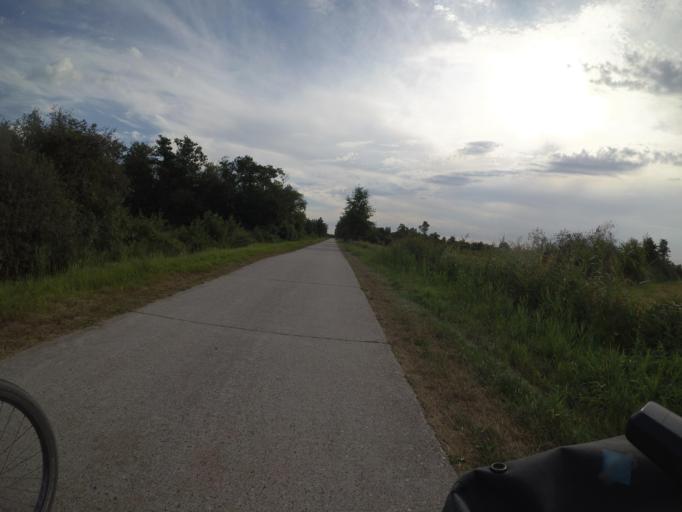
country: NL
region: Overijssel
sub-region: Gemeente Zwartewaterland
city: Hasselt
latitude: 52.6397
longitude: 6.1137
